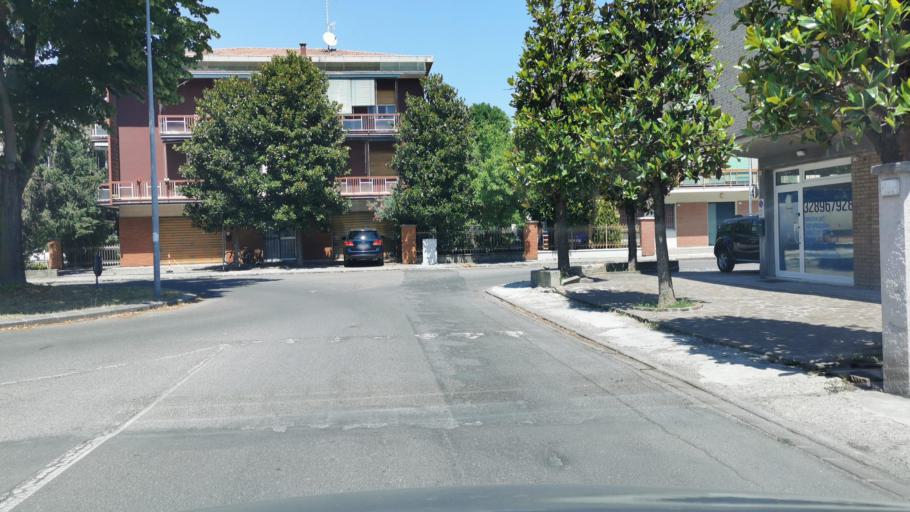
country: IT
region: Emilia-Romagna
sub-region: Provincia di Modena
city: Carpi Centro
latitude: 44.7910
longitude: 10.8874
